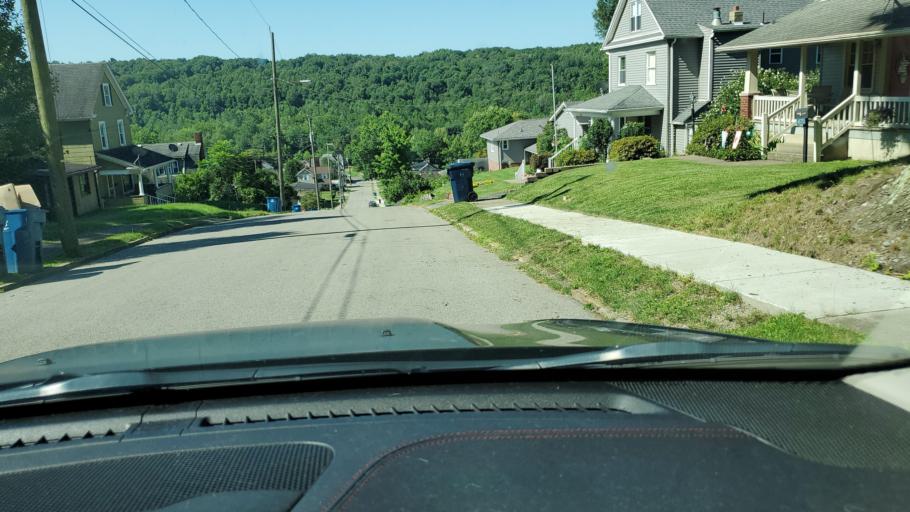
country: US
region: Ohio
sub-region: Mahoning County
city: Lowellville
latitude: 41.0426
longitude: -80.5381
